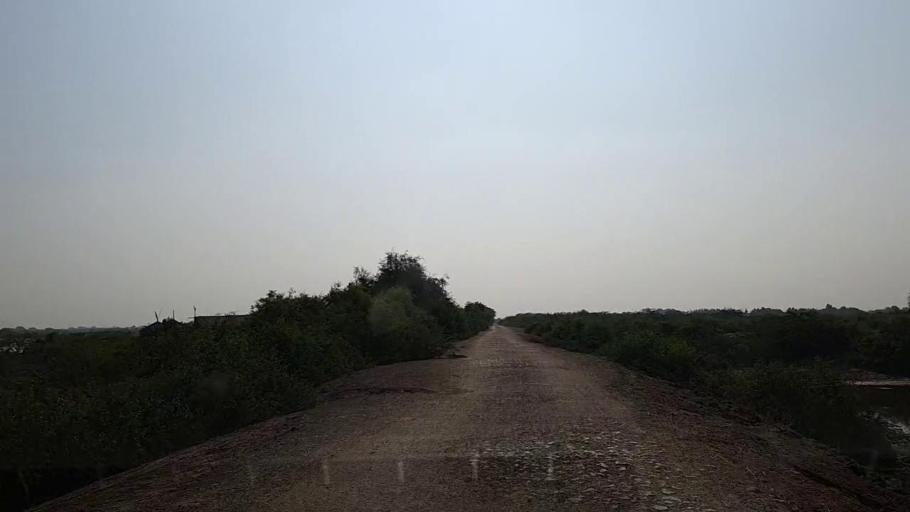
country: PK
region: Sindh
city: Mirpur Sakro
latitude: 24.6347
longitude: 67.6596
